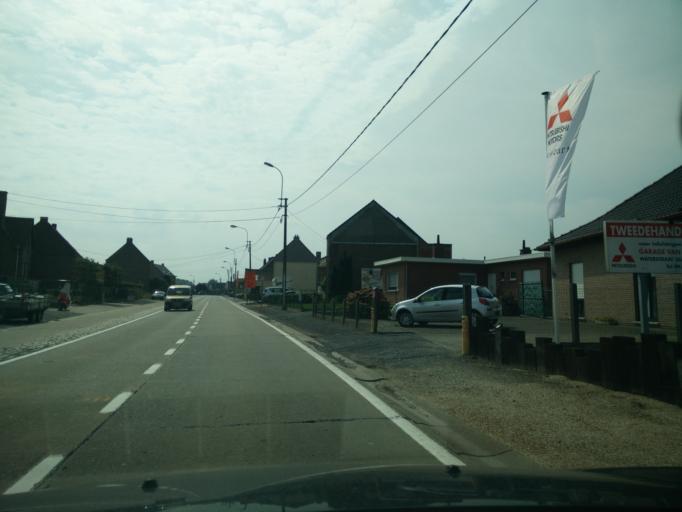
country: BE
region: Flanders
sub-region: Provincie Oost-Vlaanderen
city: Merelbeke
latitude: 50.9726
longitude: 3.7366
